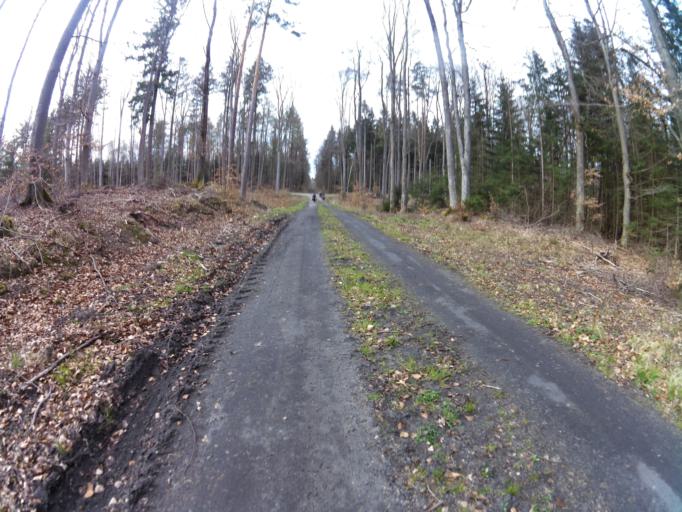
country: PL
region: West Pomeranian Voivodeship
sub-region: Powiat szczecinecki
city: Bialy Bor
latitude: 53.8925
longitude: 16.7179
